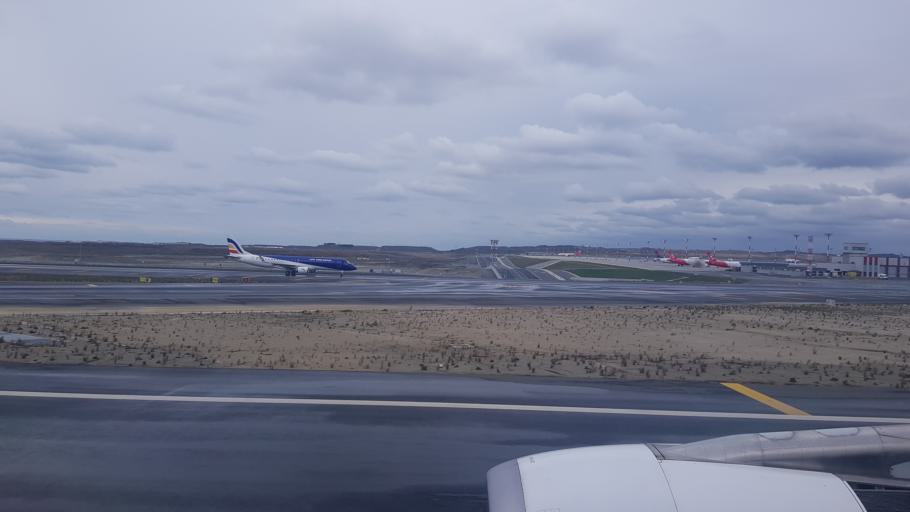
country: TR
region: Istanbul
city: Durusu
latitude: 41.2768
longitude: 28.7270
